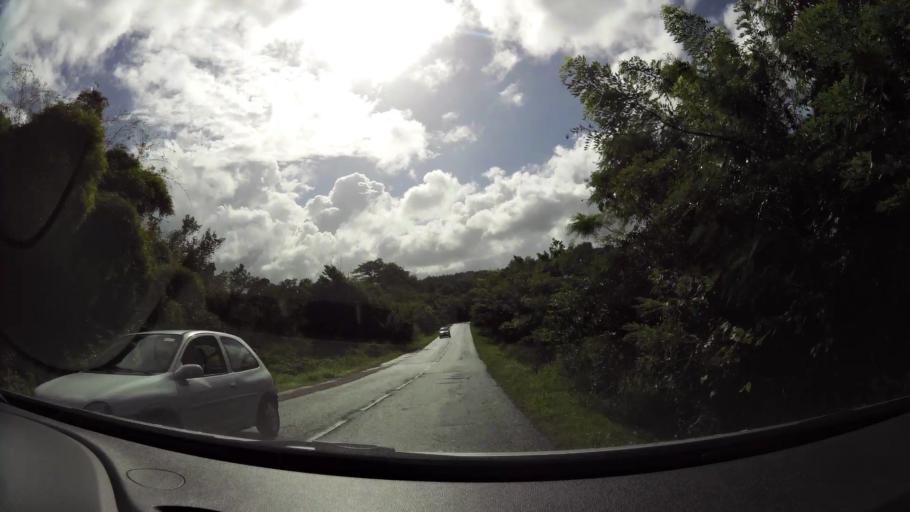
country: MQ
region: Martinique
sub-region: Martinique
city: Les Trois-Ilets
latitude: 14.5405
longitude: -61.0475
